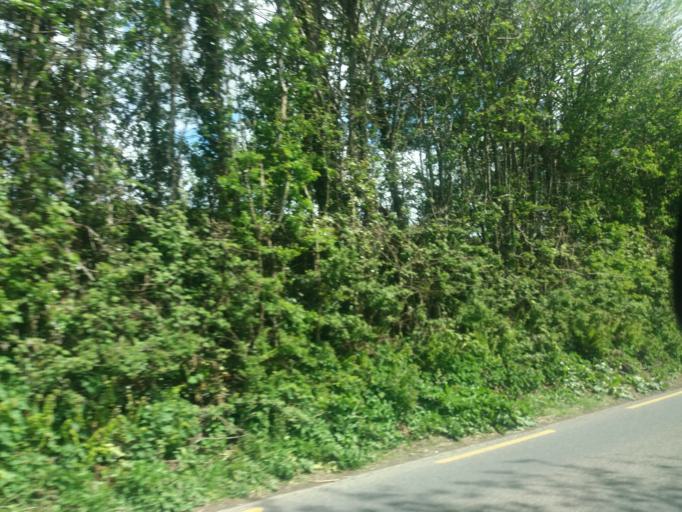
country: IE
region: Leinster
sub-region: Loch Garman
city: New Ross
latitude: 52.2665
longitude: -6.7694
